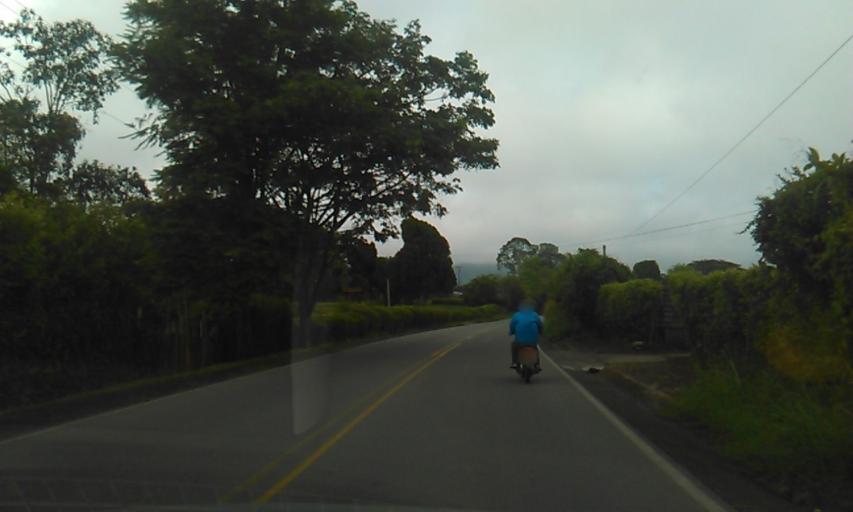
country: CO
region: Quindio
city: Cordoba
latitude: 4.4178
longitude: -75.7234
